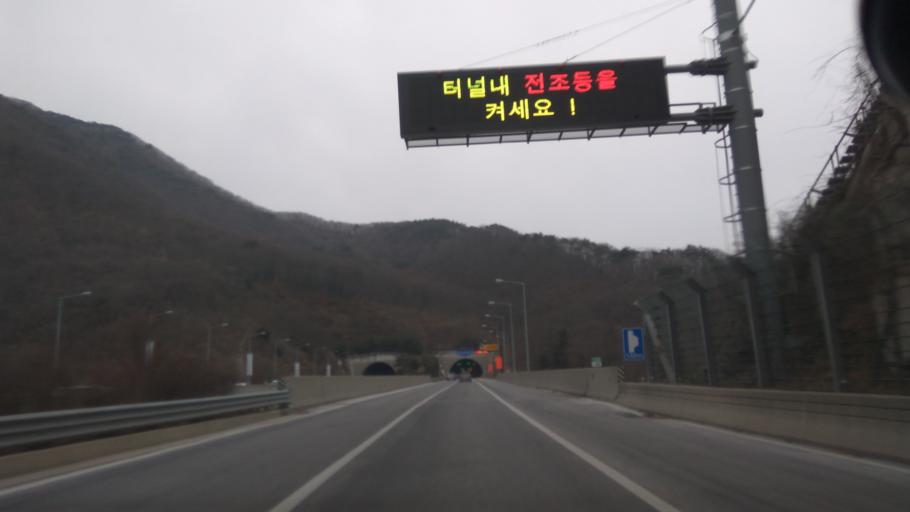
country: KR
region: Gyeonggi-do
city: Cheongpyeong
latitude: 37.6499
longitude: 127.4591
